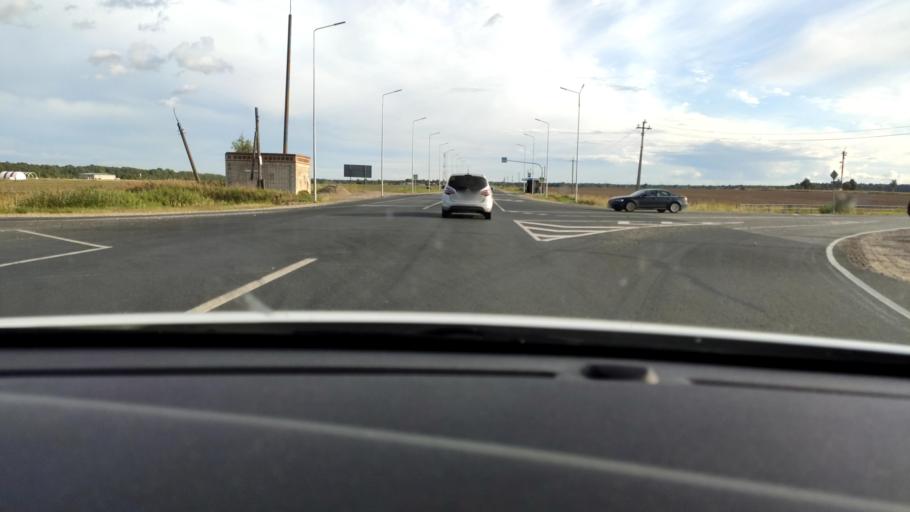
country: RU
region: Mariy-El
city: Suslonger
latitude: 56.2150
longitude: 48.2368
